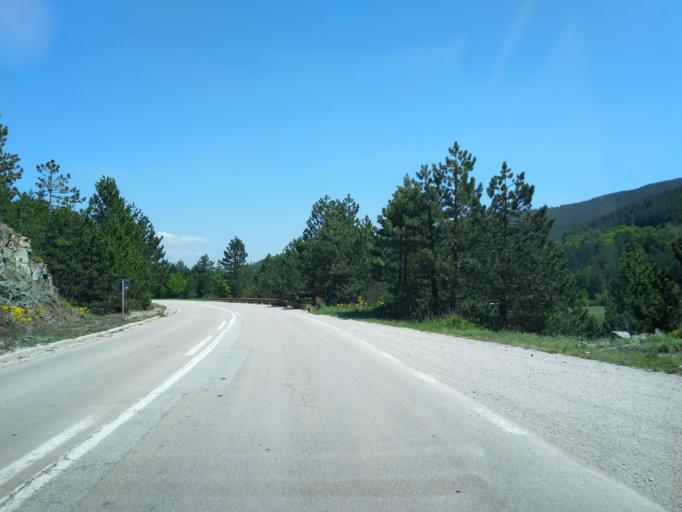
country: RS
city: Durici
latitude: 43.8310
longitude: 19.5329
